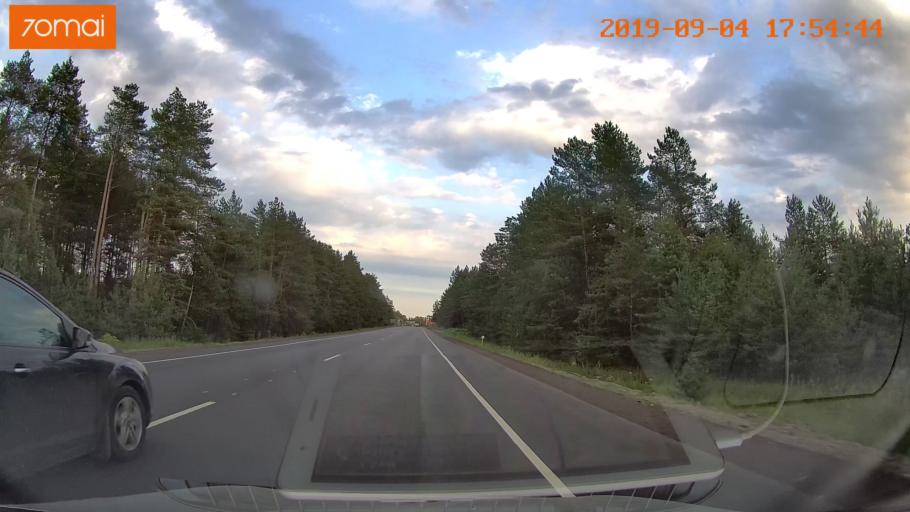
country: RU
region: Moskovskaya
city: Imeni Tsyurupy
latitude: 55.5089
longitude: 38.7531
